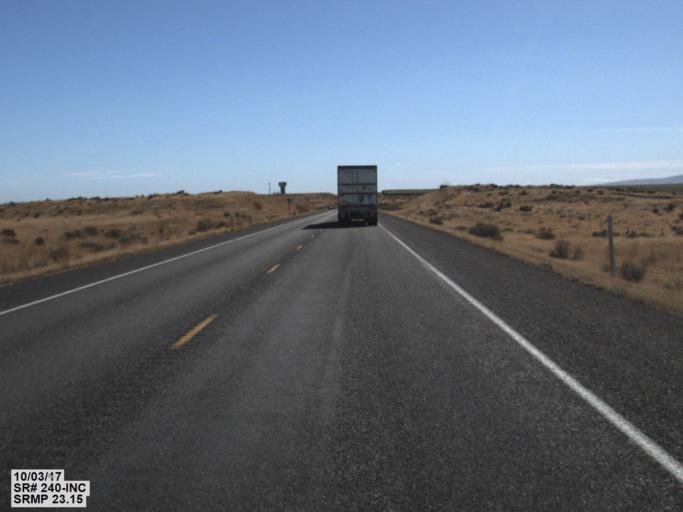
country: US
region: Washington
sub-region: Benton County
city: West Richland
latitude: 46.3593
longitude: -119.3788
